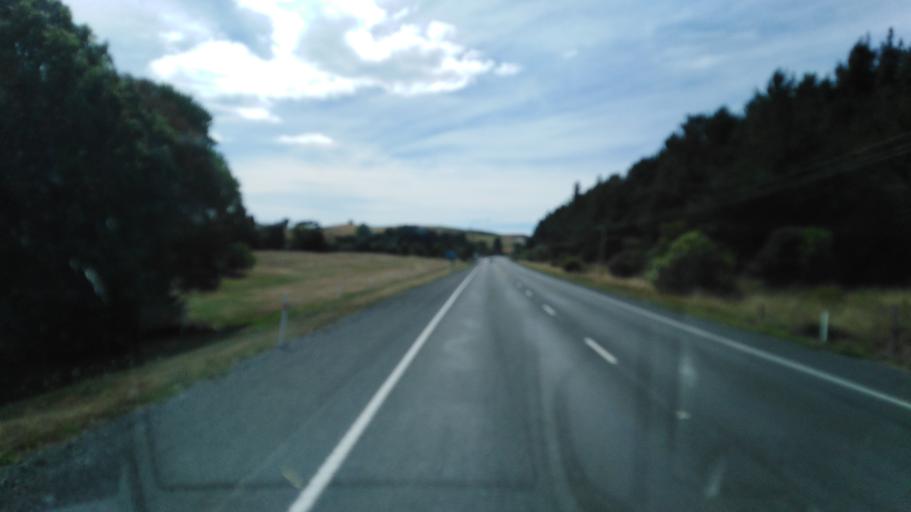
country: NZ
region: Canterbury
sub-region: Kaikoura District
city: Kaikoura
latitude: -42.4139
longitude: 173.6402
